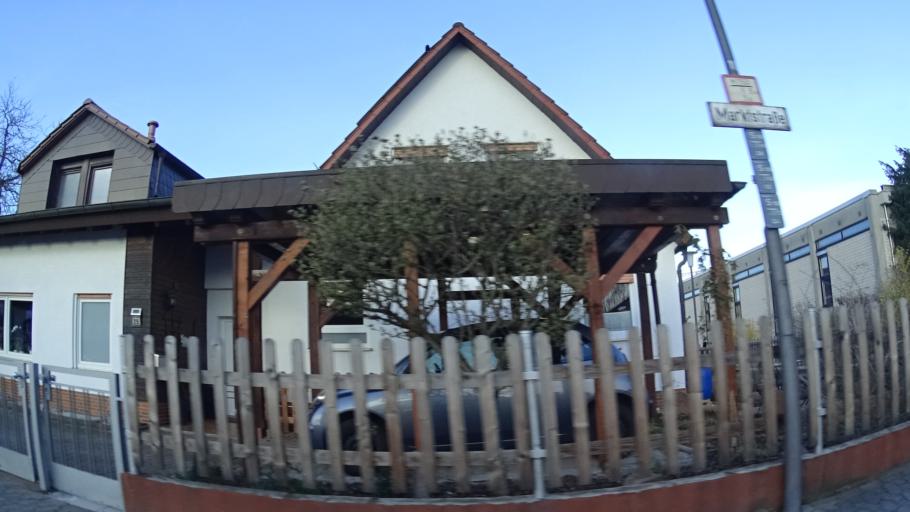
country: DE
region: Baden-Wuerttemberg
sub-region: Karlsruhe Region
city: Eppelheim
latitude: 49.3991
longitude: 8.6481
